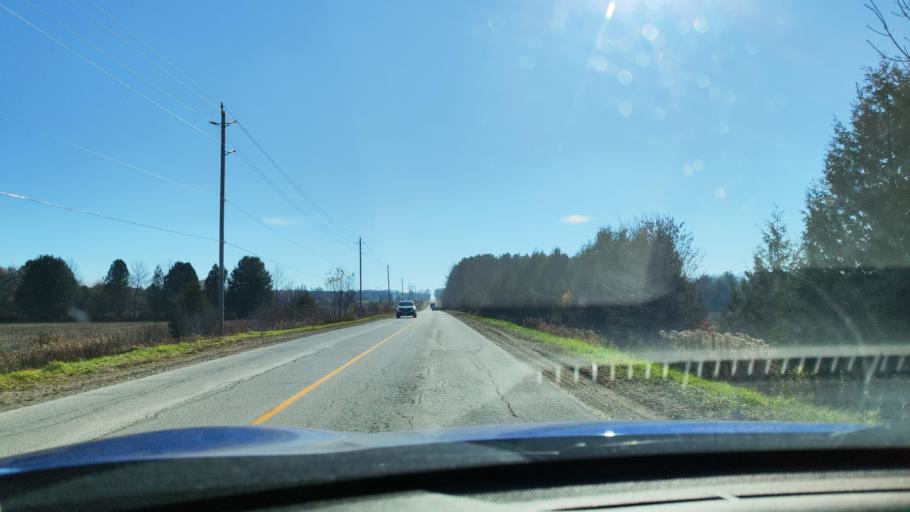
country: CA
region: Ontario
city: Wasaga Beach
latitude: 44.4678
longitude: -80.0052
